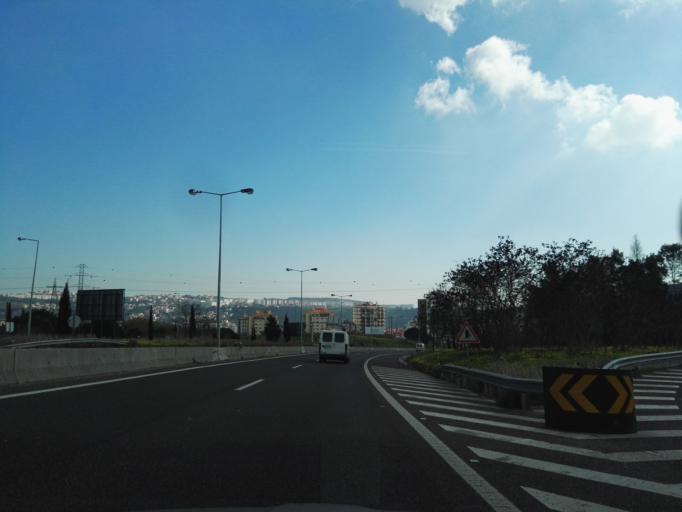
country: PT
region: Lisbon
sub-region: Odivelas
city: Odivelas
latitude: 38.8018
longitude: -9.1778
